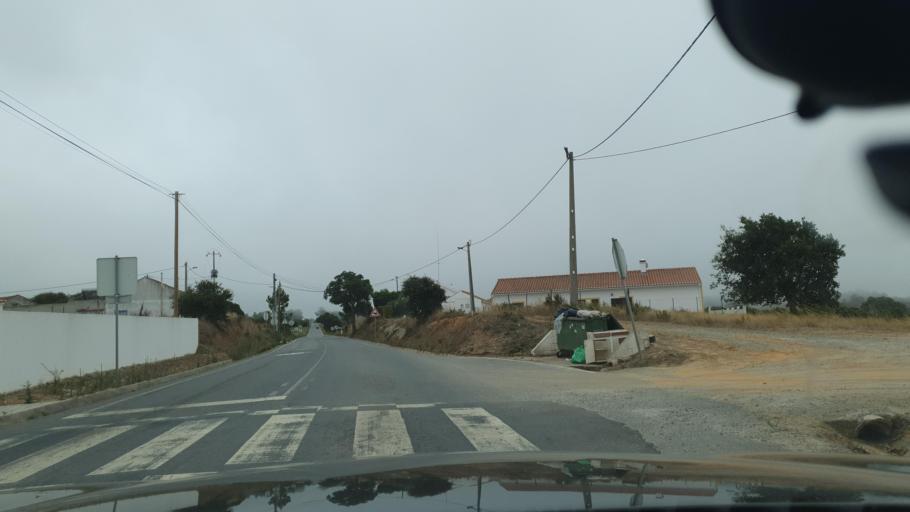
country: PT
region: Beja
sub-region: Odemira
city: Sao Teotonio
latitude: 37.5321
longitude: -8.7171
